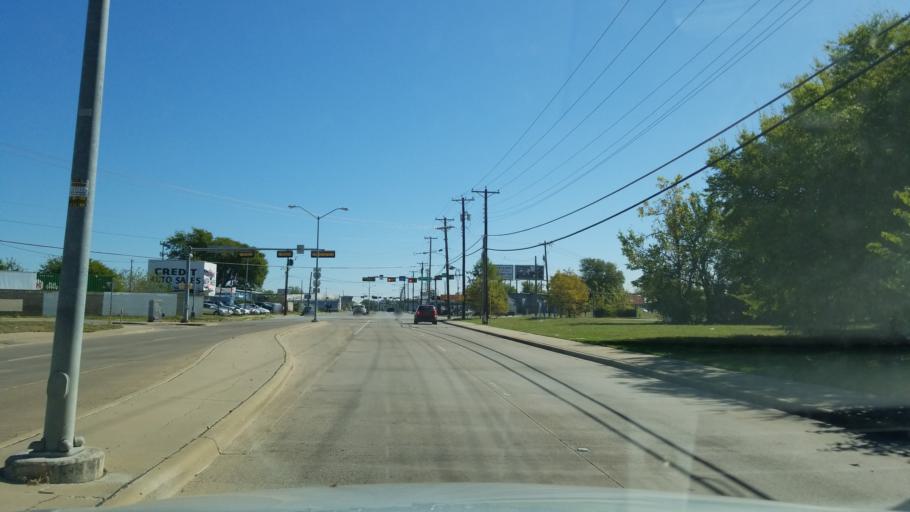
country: US
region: Texas
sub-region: Dallas County
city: Dallas
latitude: 32.7834
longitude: -96.7514
